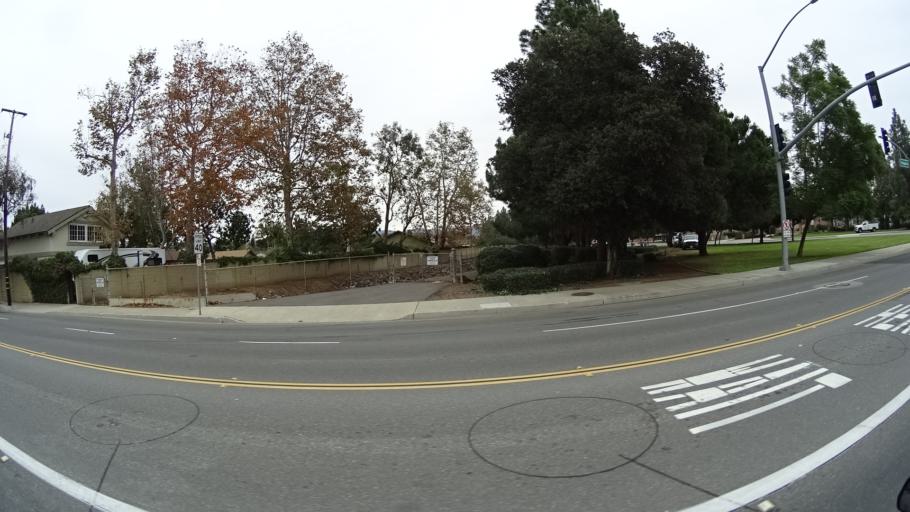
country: US
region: California
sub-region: Orange County
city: Tustin
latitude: 33.7518
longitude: -117.8225
